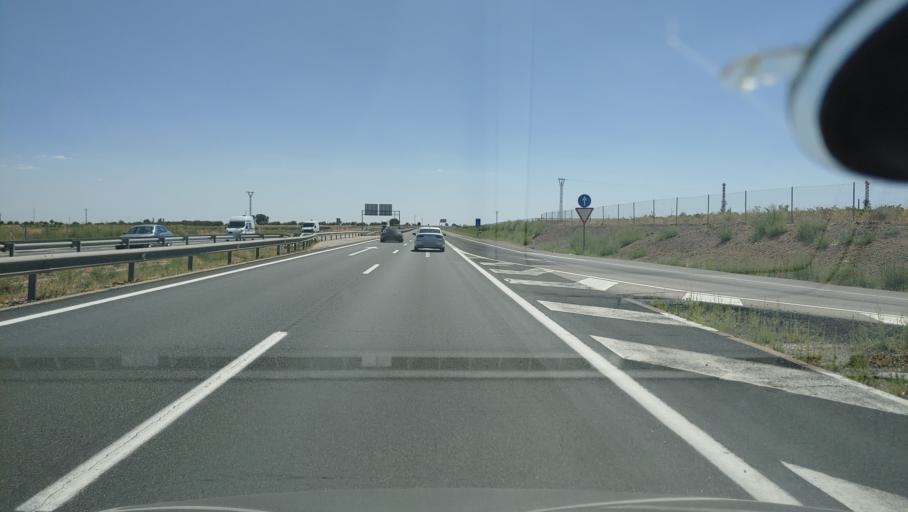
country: ES
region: Castille-La Mancha
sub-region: Provincia de Ciudad Real
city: Villarta de San Juan
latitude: 39.2340
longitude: -3.4115
